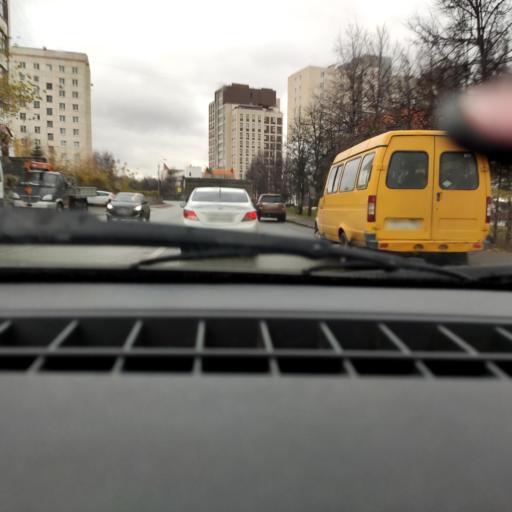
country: RU
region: Bashkortostan
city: Ufa
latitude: 54.7797
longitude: 56.0229
